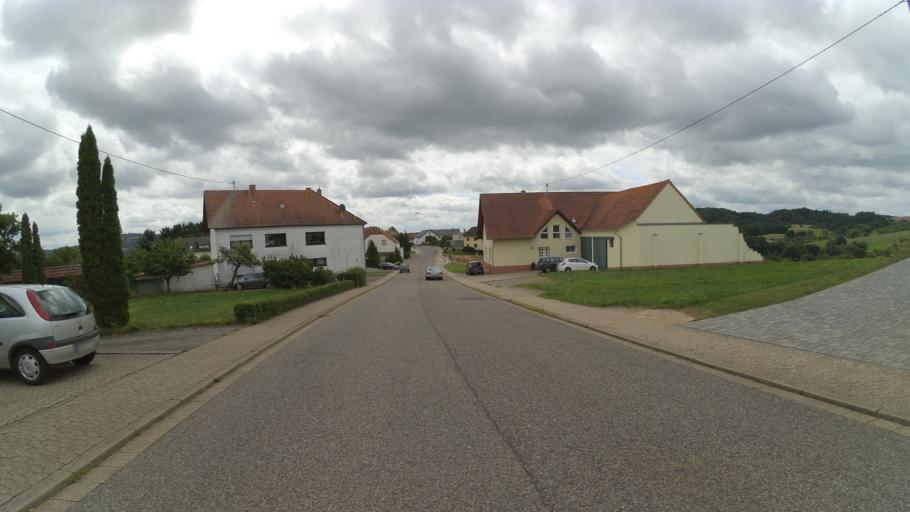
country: DE
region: Saarland
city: Tholey
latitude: 49.4969
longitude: 6.9712
